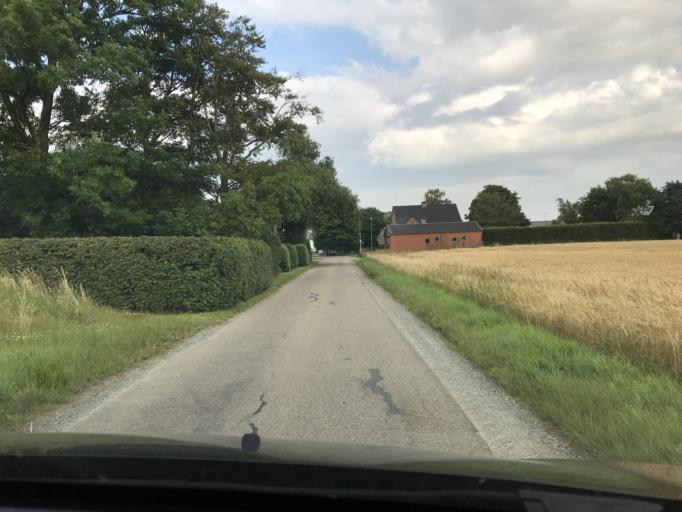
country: DK
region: South Denmark
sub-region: Vejle Kommune
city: Jelling
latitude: 55.8056
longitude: 9.4279
